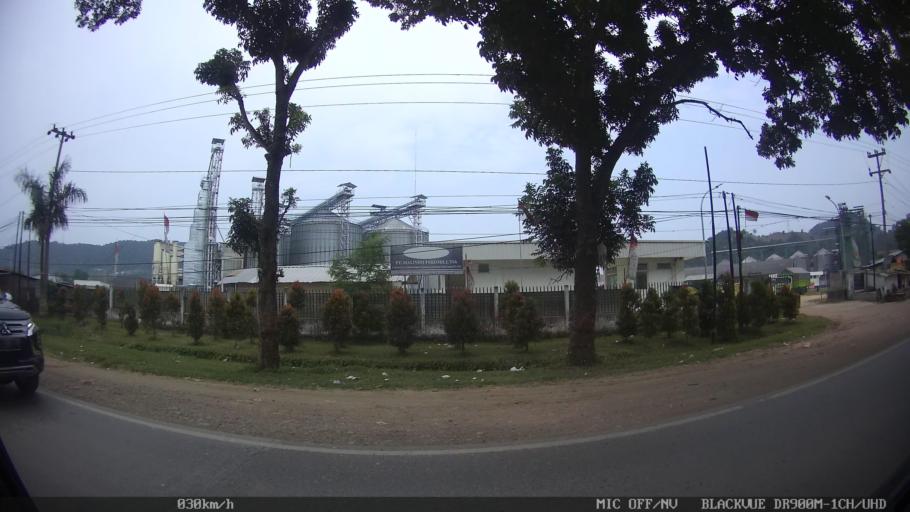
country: ID
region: Lampung
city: Panjang
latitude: -5.4219
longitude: 105.3329
